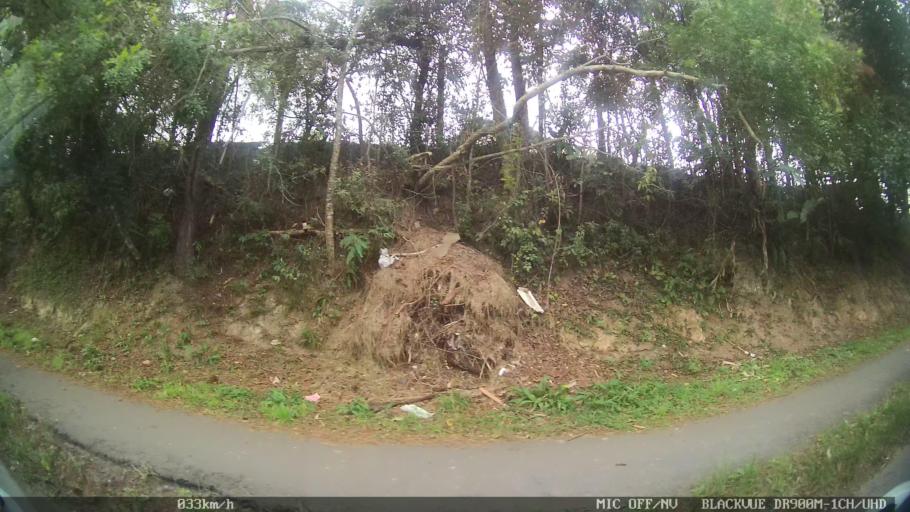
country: BR
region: Parana
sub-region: Colombo
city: Colombo
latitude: -25.3592
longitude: -49.2429
